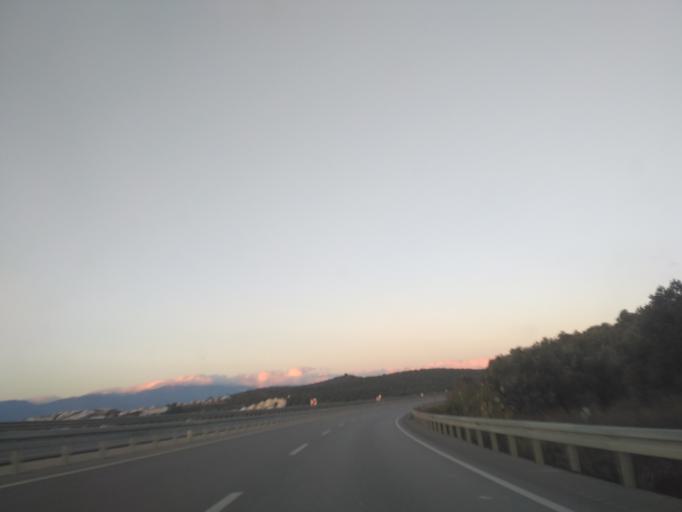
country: TR
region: Balikesir
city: Emrutabat
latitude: 39.4399
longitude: 26.8625
